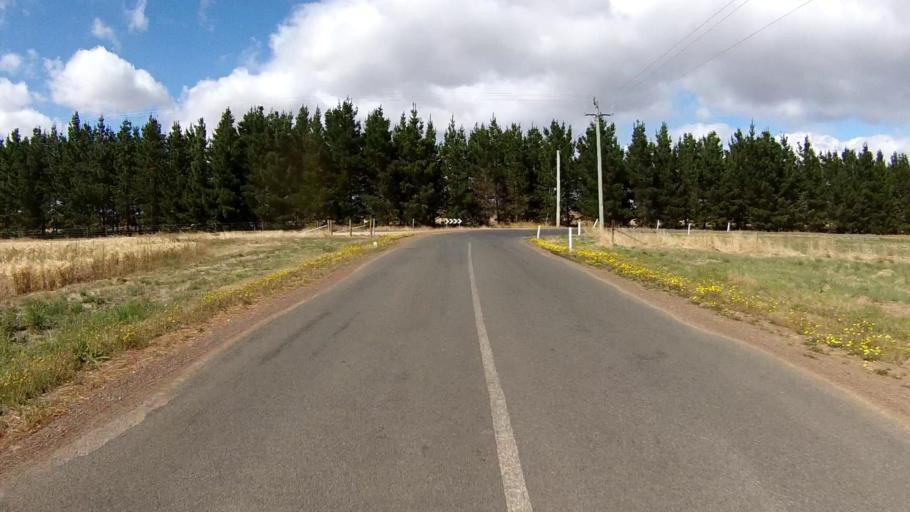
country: AU
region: Tasmania
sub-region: Northern Midlands
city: Evandale
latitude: -41.7767
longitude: 147.4732
